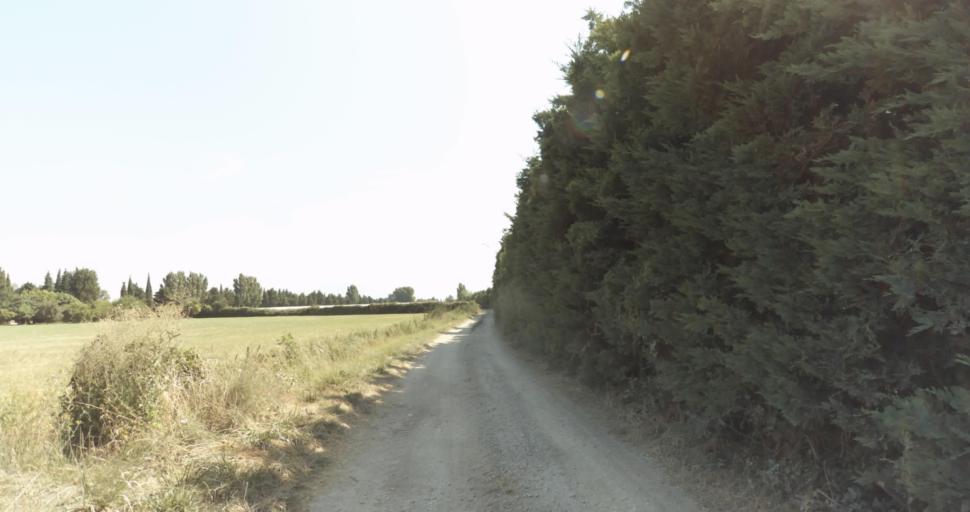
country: FR
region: Provence-Alpes-Cote d'Azur
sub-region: Departement du Vaucluse
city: Monteux
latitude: 44.0199
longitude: 5.0131
